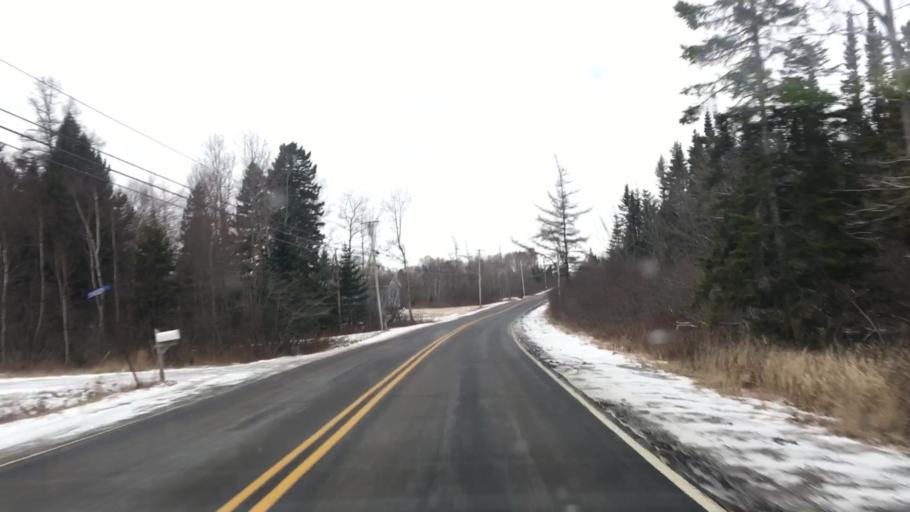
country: US
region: Maine
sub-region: Washington County
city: Machiasport
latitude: 44.7017
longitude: -67.3449
